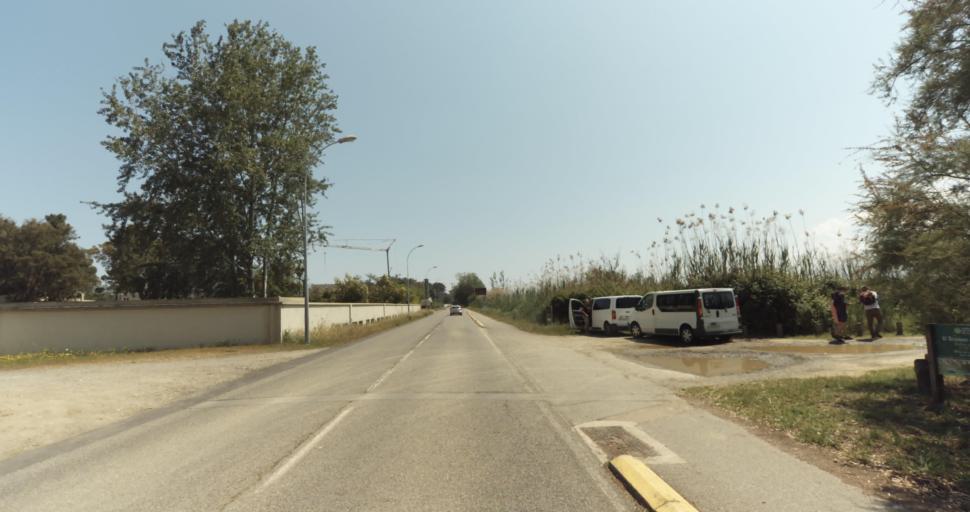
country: FR
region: Corsica
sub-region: Departement de la Haute-Corse
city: Biguglia
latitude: 42.6113
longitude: 9.4822
